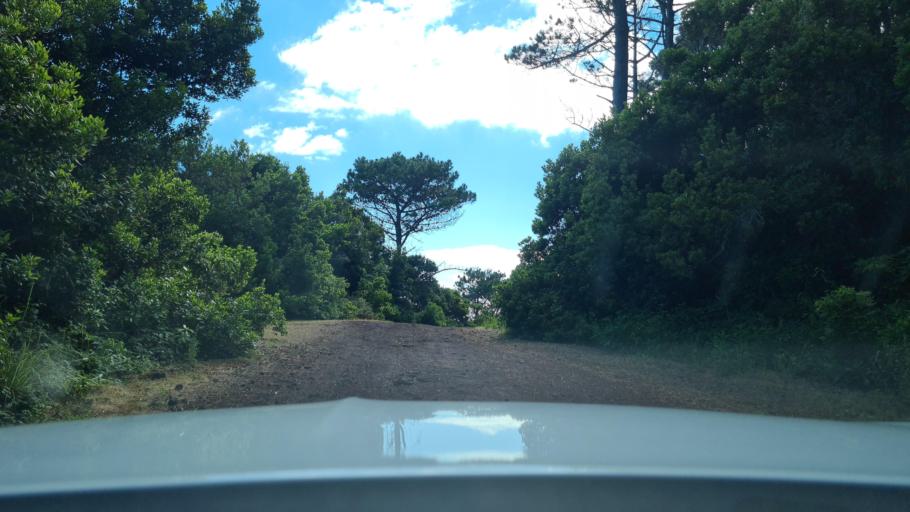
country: PT
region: Azores
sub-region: Sao Roque do Pico
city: Sao Roque do Pico
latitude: 38.4115
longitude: -28.3034
